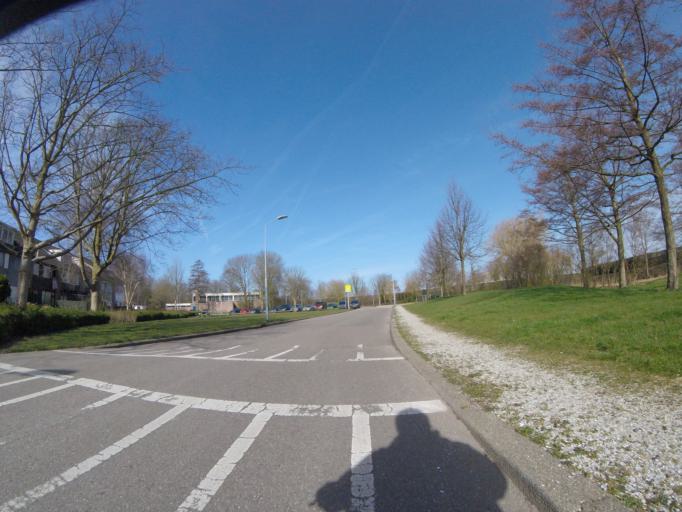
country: NL
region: North Holland
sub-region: Gemeente Bloemendaal
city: Bennebroek
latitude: 52.3136
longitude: 4.6205
